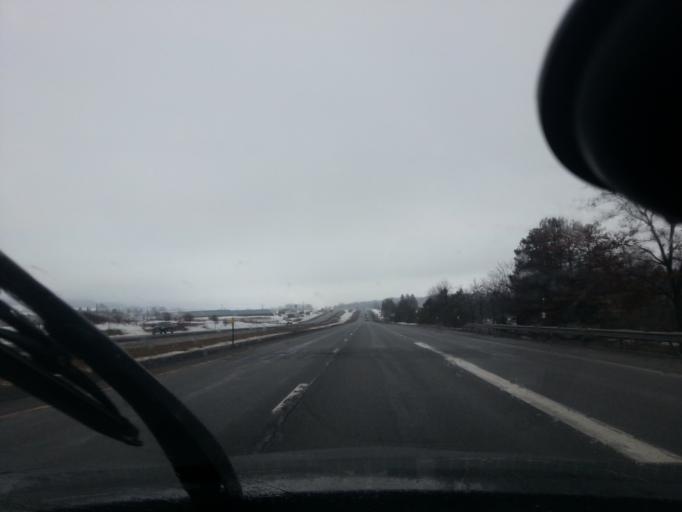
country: US
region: New York
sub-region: Cortland County
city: Homer
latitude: 42.7955
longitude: -76.1239
